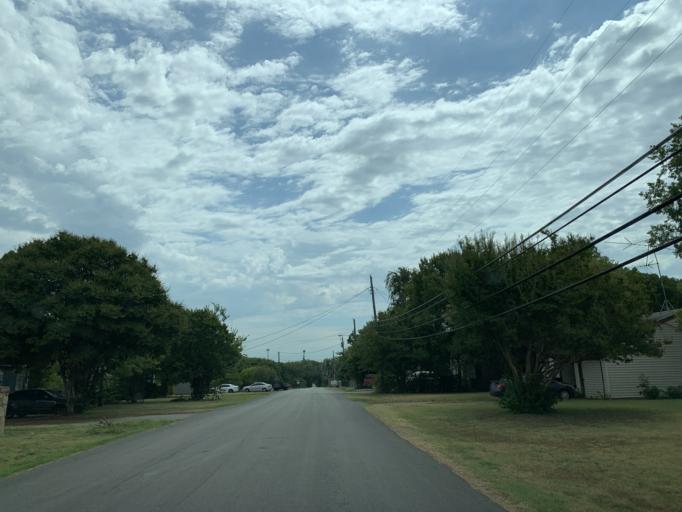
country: US
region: Texas
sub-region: Dallas County
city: Duncanville
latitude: 32.6724
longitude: -96.8311
